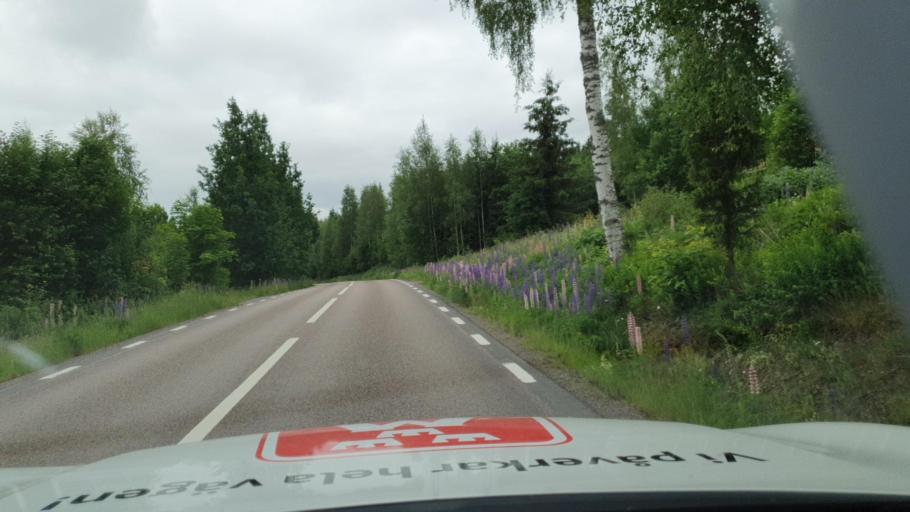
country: SE
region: Vaermland
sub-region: Torsby Kommun
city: Torsby
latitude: 59.9187
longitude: 12.8978
